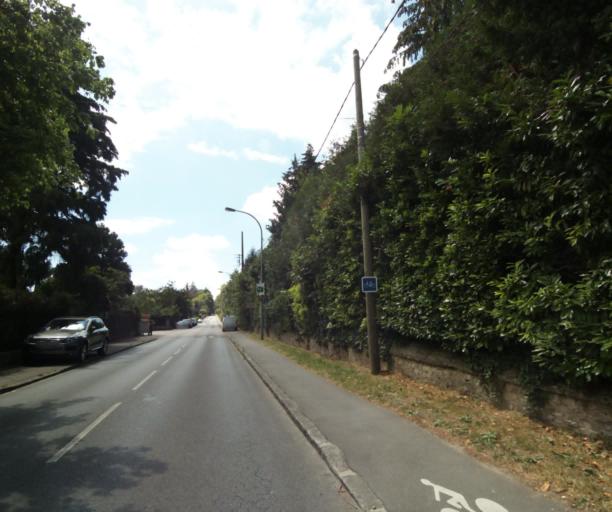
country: FR
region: Ile-de-France
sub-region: Departement de Seine-et-Marne
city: Chartrettes
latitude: 48.4801
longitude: 2.6949
